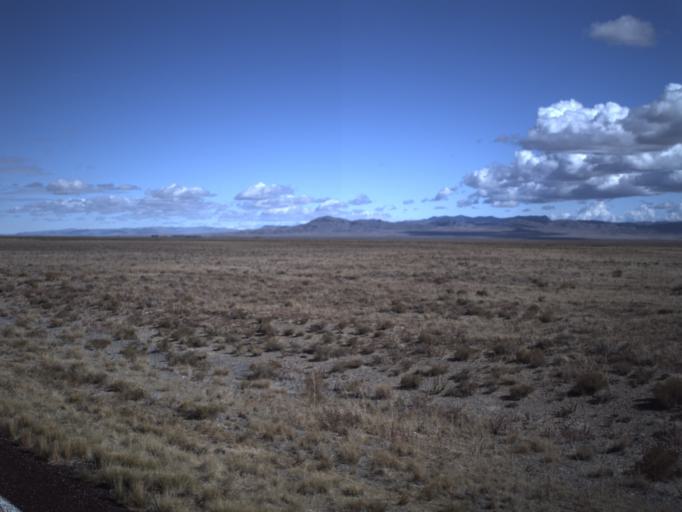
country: US
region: Nevada
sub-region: White Pine County
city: McGill
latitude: 38.9771
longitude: -114.0340
